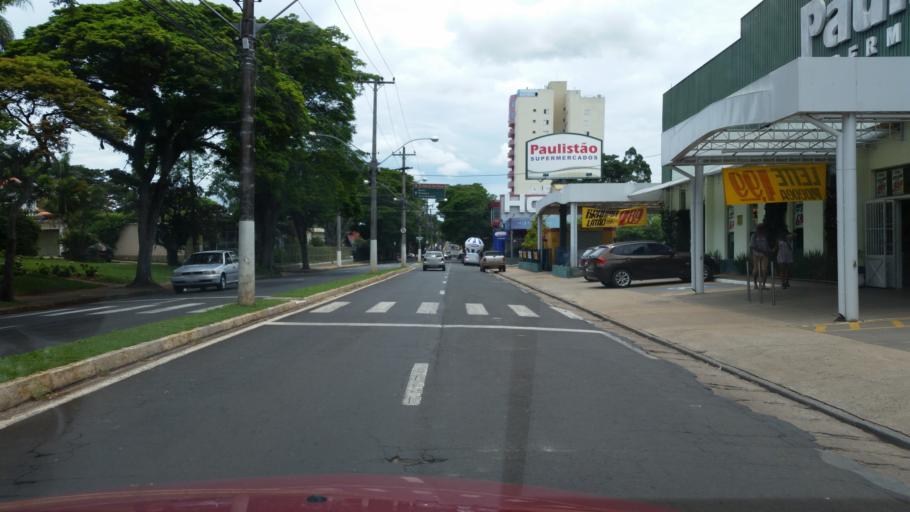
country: BR
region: Sao Paulo
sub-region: Avare
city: Avare
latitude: -23.0973
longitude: -48.9330
